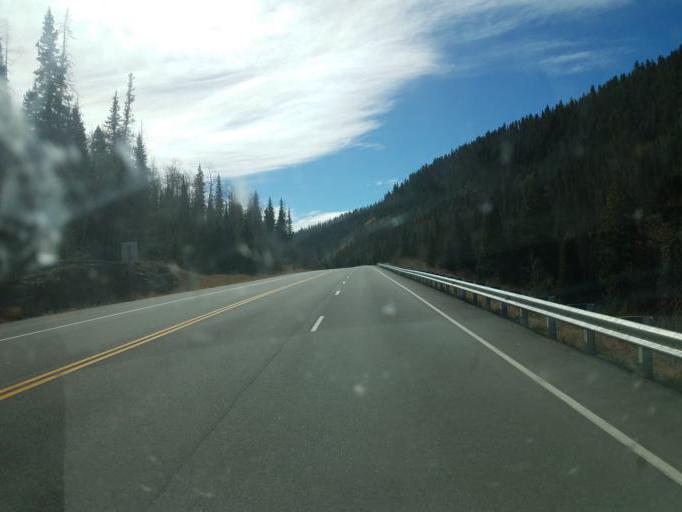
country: US
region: Colorado
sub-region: Mineral County
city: Creede
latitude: 37.5412
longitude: -106.7723
